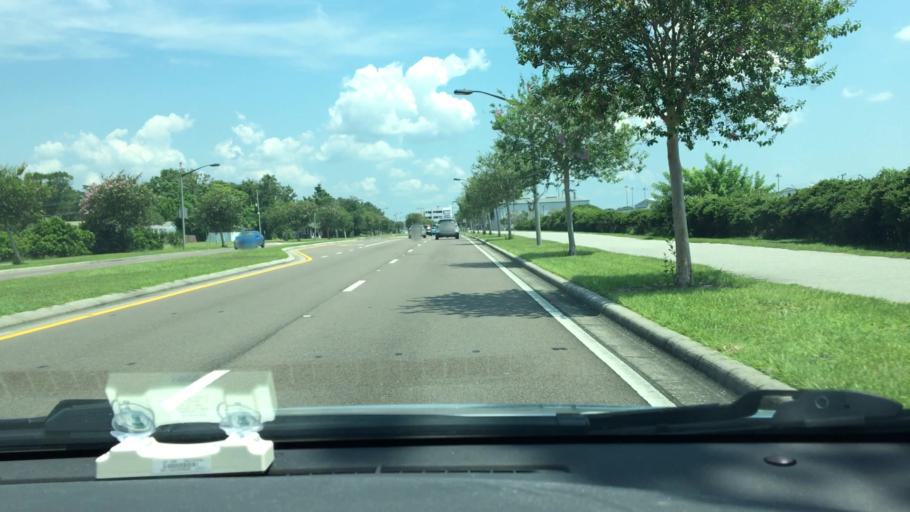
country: US
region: Florida
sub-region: Orange County
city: Orlando
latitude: 28.5415
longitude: -81.3436
